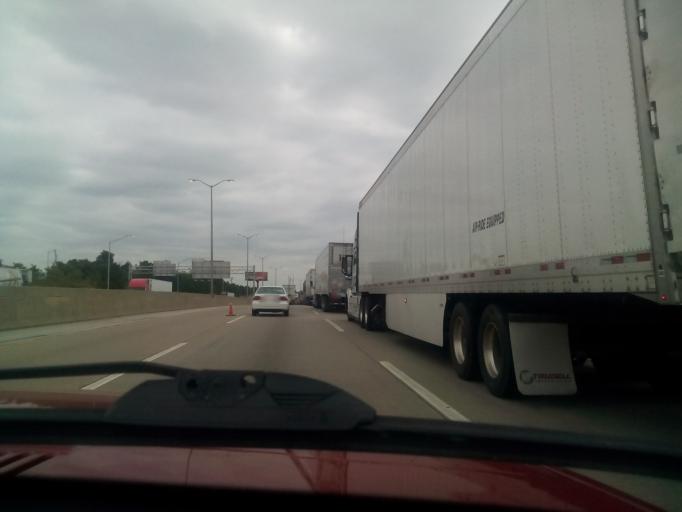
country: US
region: Illinois
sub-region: Cook County
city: East Hazel Crest
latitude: 41.5787
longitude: -87.6307
